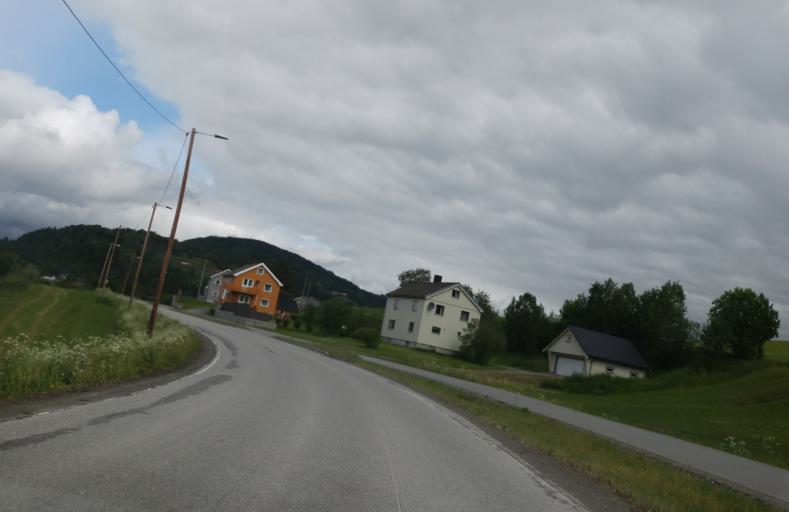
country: NO
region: Sor-Trondelag
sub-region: Selbu
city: Mebonden
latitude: 63.2449
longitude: 11.0907
